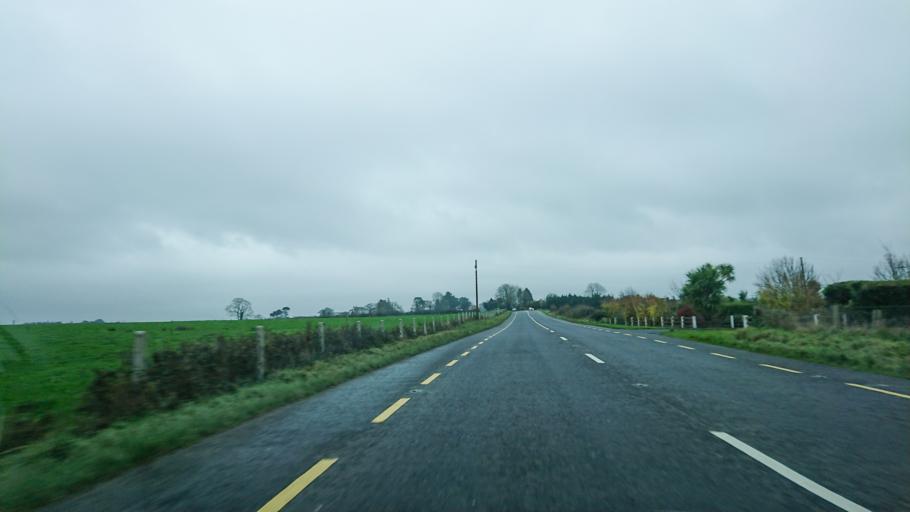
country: IE
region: Leinster
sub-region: Kilkenny
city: Mooncoin
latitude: 52.2842
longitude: -7.2110
